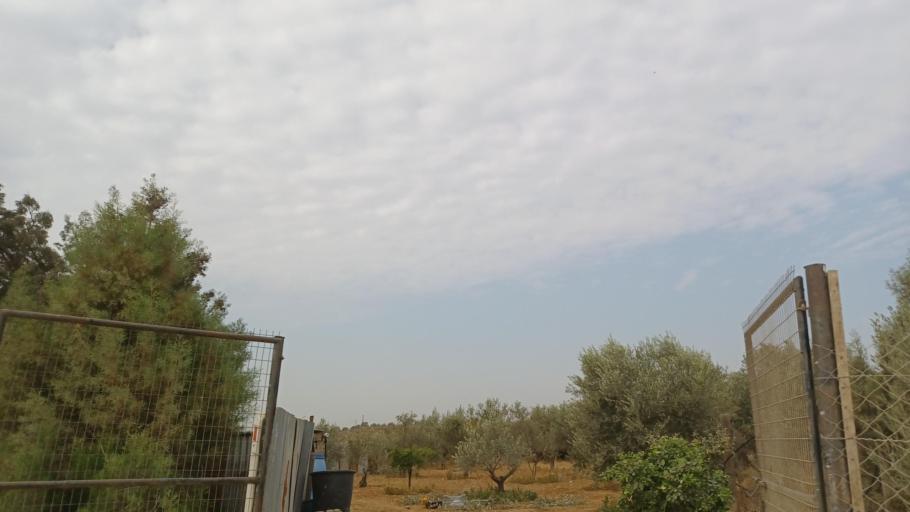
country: CY
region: Larnaka
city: Kolossi
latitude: 34.6682
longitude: 32.9499
